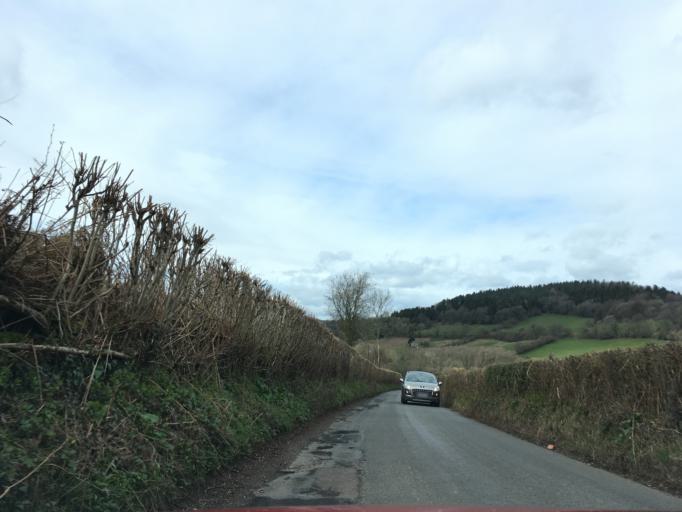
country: GB
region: England
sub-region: Gloucestershire
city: Coleford
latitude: 51.7755
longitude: -2.6336
